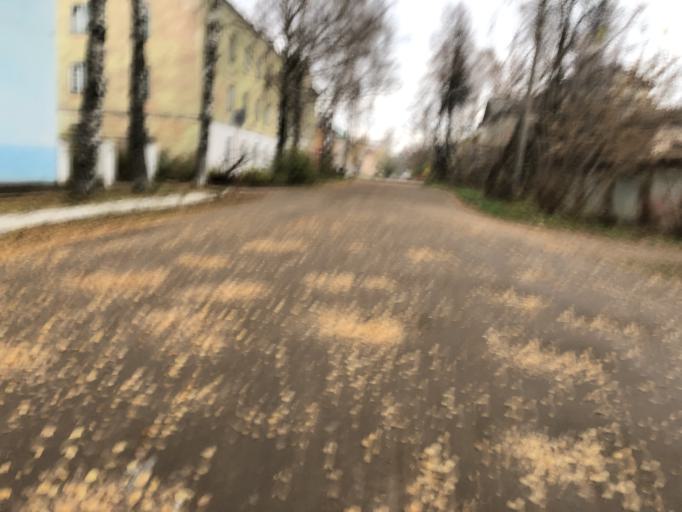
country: RU
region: Tverskaya
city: Rzhev
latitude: 56.2561
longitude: 34.3245
